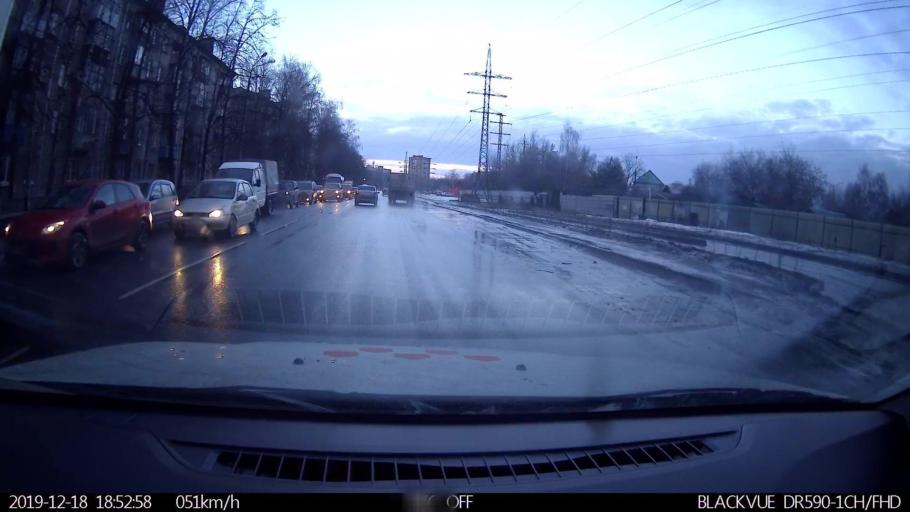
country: RU
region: Nizjnij Novgorod
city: Gorbatovka
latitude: 56.3331
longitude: 43.8565
